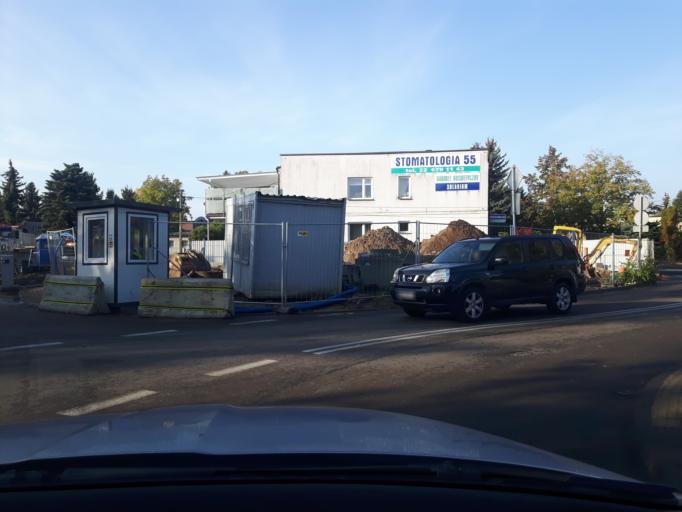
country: PL
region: Masovian Voivodeship
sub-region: Warszawa
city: Targowek
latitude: 52.2851
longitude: 21.0622
